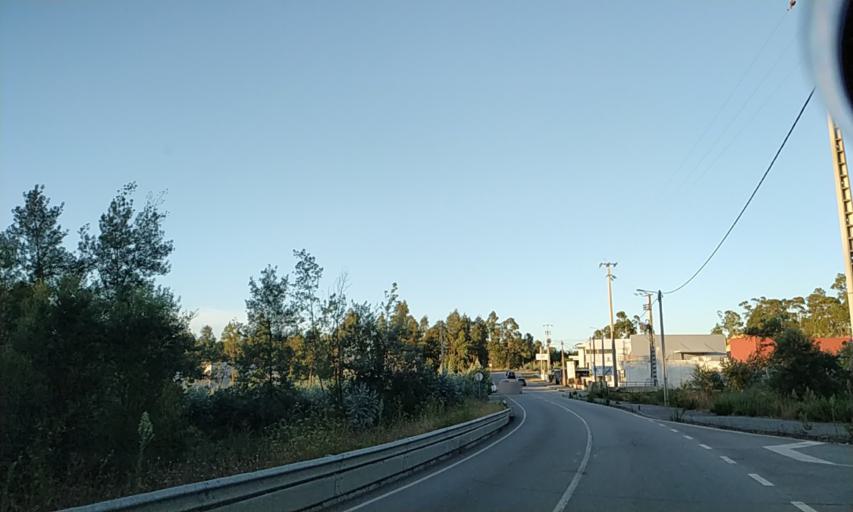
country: PT
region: Aveiro
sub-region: Oliveira do Bairro
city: Oia
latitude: 40.5439
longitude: -8.5257
